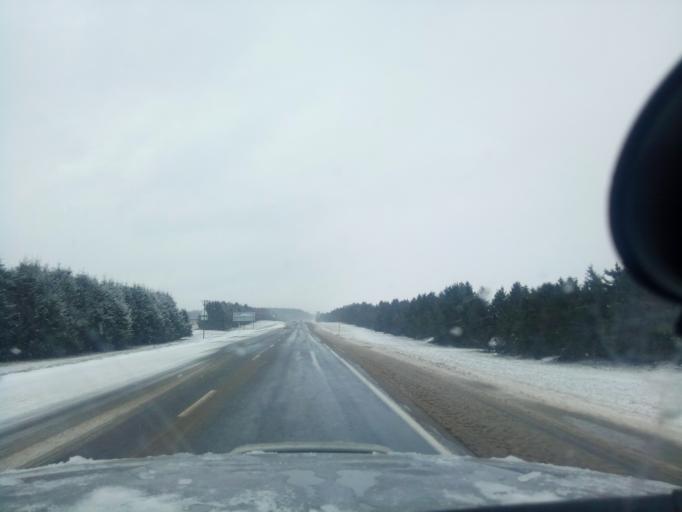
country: BY
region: Minsk
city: Haradzyeya
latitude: 53.2916
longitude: 26.5776
